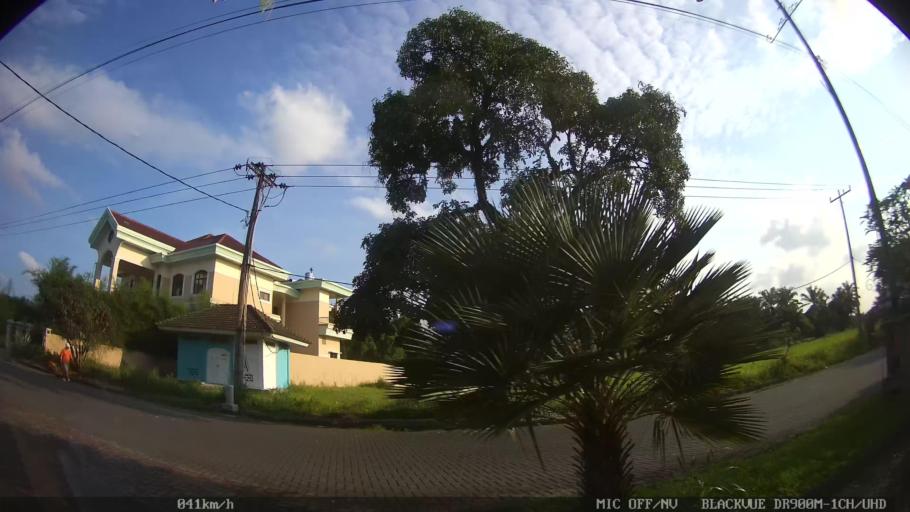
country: ID
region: North Sumatra
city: Medan
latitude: 3.6251
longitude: 98.6503
